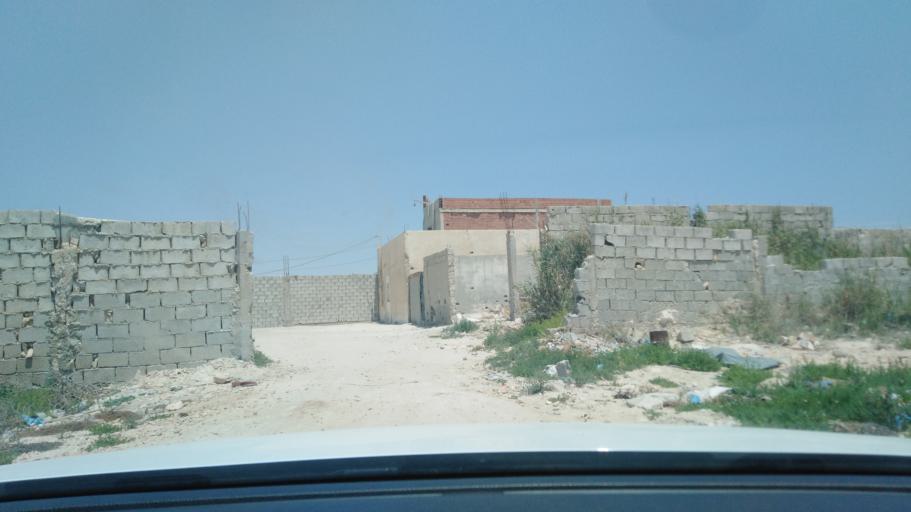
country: TN
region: Qabis
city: Gabes
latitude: 33.9452
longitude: 10.0756
